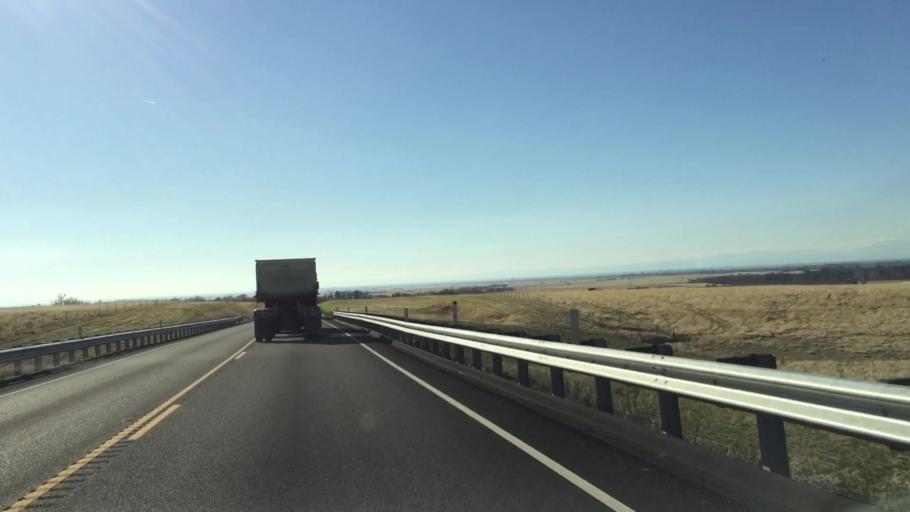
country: US
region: California
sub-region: Butte County
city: Thermalito
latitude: 39.6159
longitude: -121.6035
